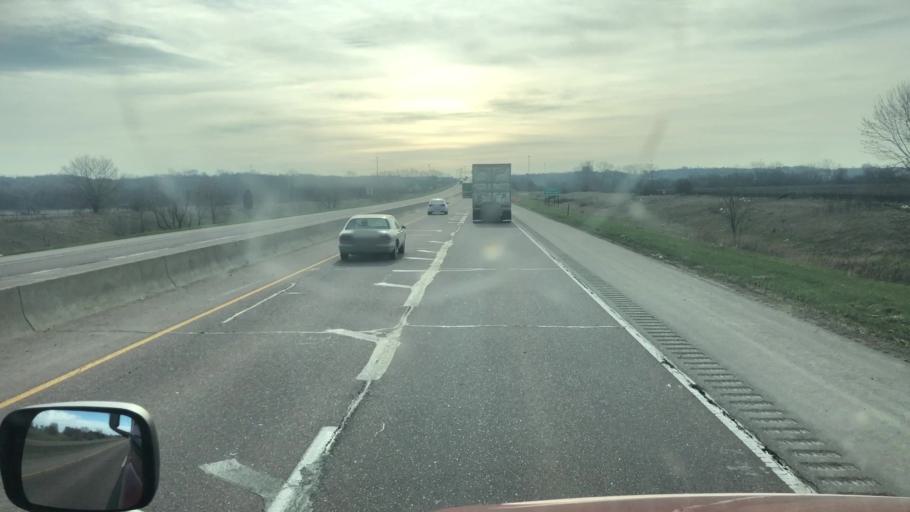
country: US
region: Nebraska
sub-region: Dakota County
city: South Sioux City
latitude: 42.4483
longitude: -96.3932
